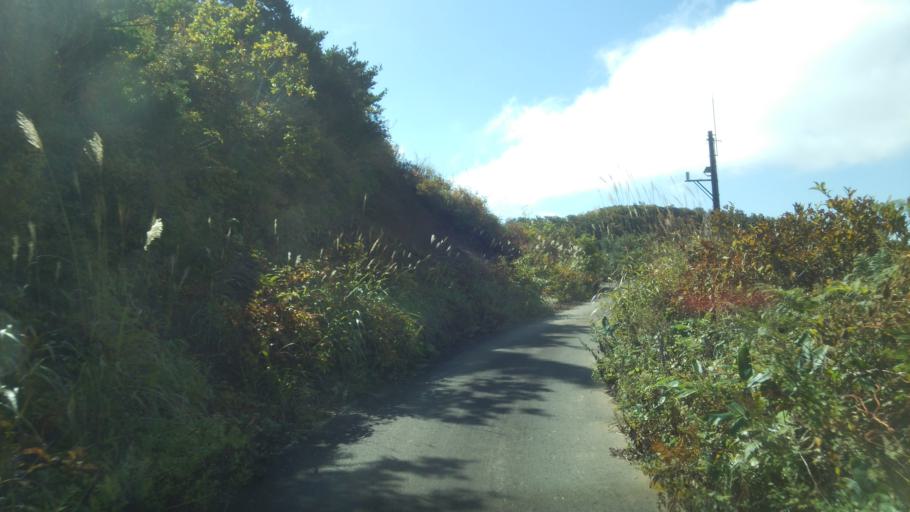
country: JP
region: Fukushima
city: Inawashiro
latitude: 37.6138
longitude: 139.9955
